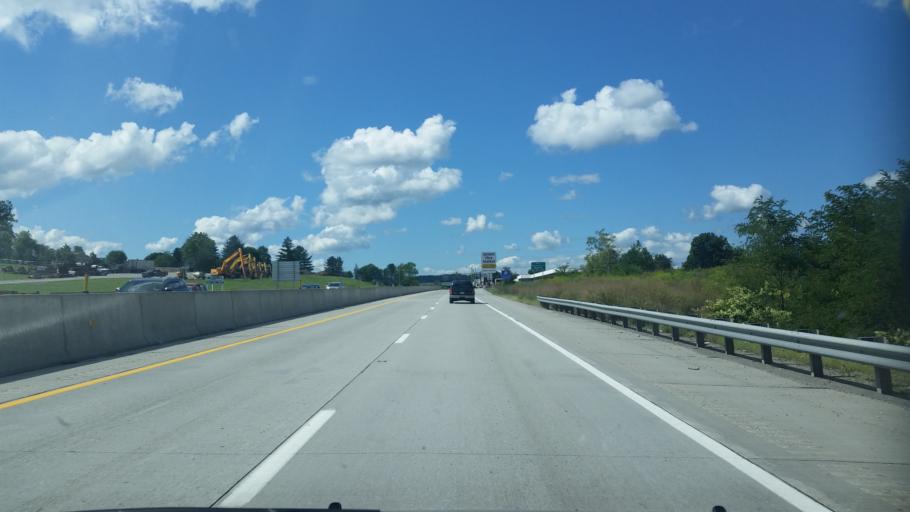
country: US
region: Pennsylvania
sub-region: Indiana County
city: Blairsville
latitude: 40.4359
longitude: -79.2776
